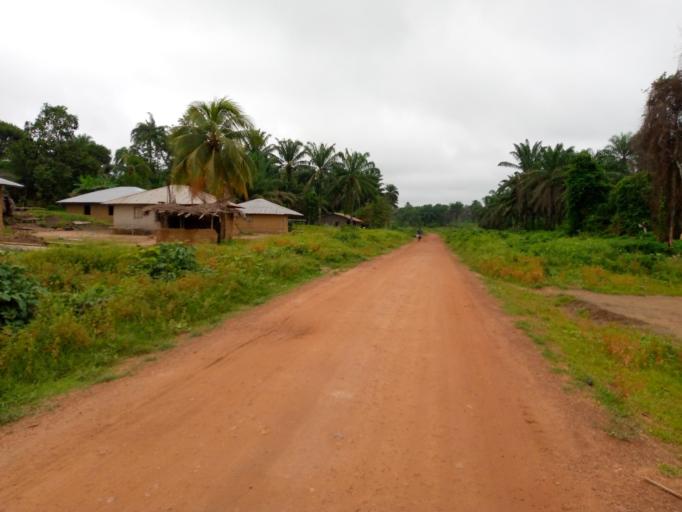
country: SL
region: Southern Province
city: Sumbuya
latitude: 7.5943
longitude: -12.0846
